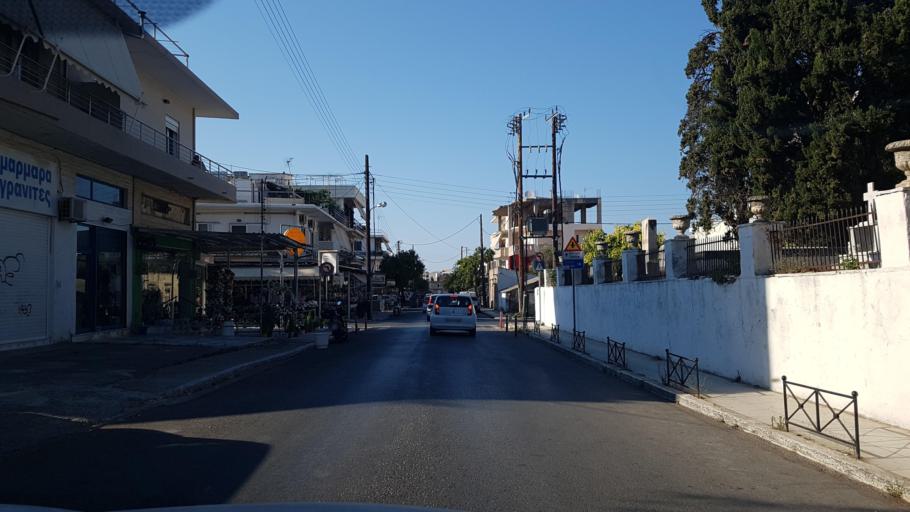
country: GR
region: Crete
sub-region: Nomos Chanias
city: Chania
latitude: 35.5076
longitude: 24.0198
